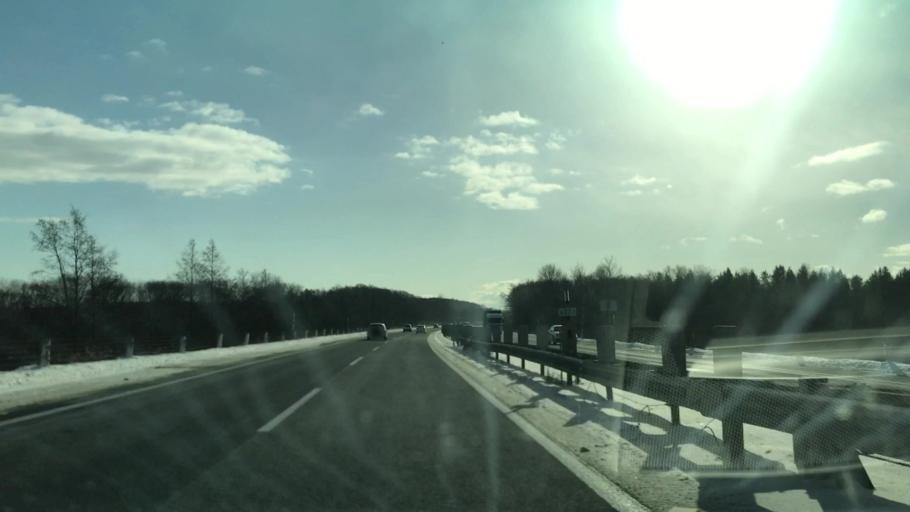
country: JP
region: Hokkaido
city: Chitose
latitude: 42.8365
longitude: 141.6059
